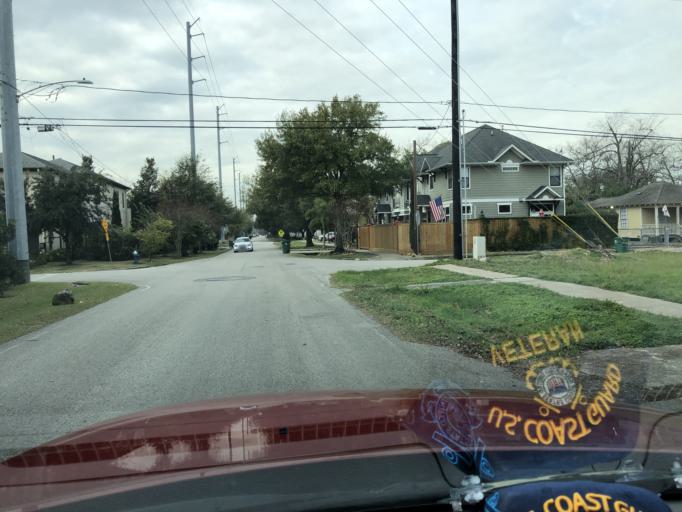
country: US
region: Texas
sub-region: Harris County
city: Houston
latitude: 29.7925
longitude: -95.4057
